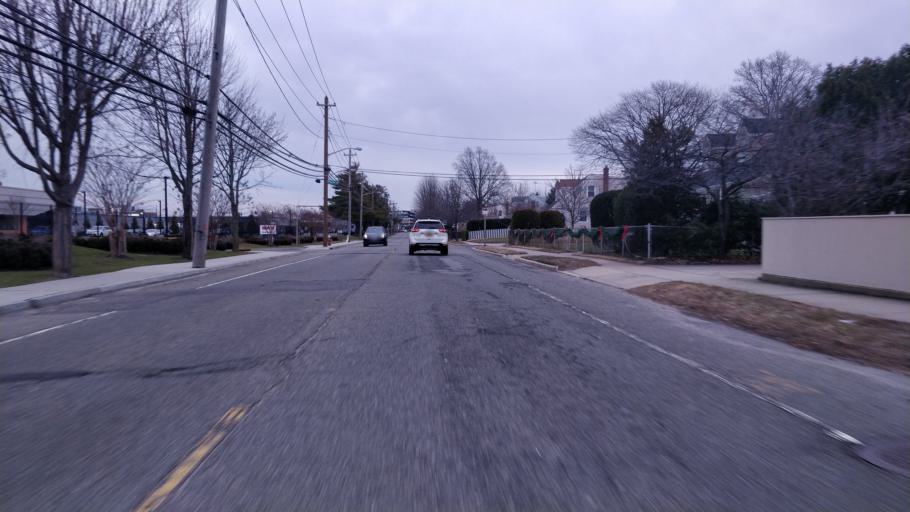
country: US
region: New York
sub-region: Nassau County
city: Hicksville
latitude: 40.7631
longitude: -73.5388
